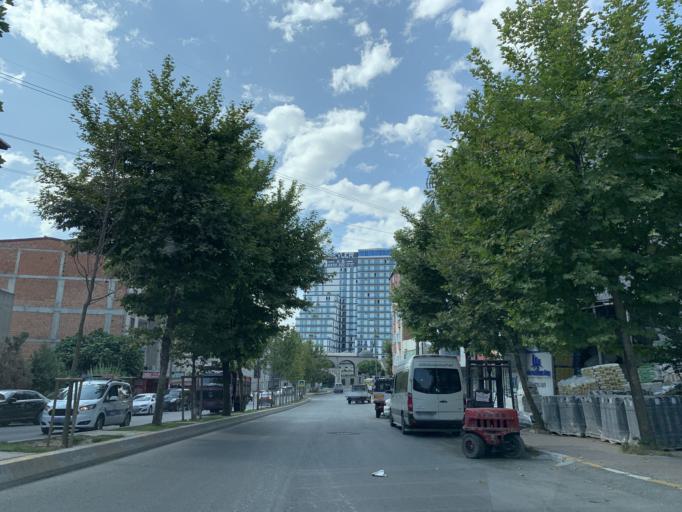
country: TR
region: Istanbul
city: Esenyurt
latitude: 41.0406
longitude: 28.6611
